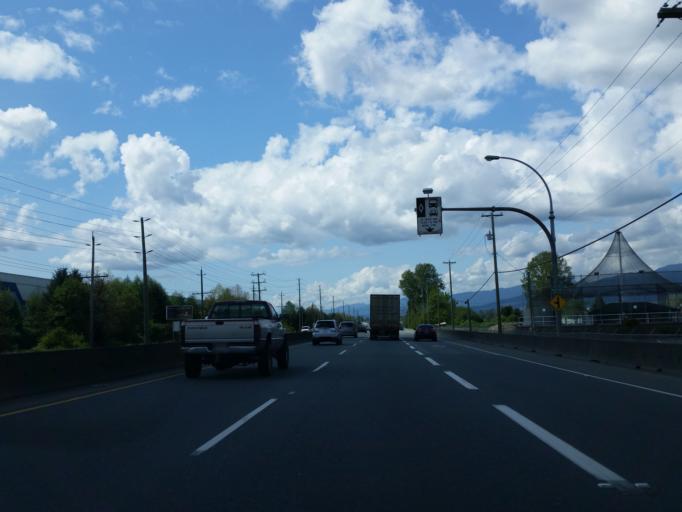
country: CA
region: British Columbia
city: Pitt Meadows
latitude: 49.2331
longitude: -122.6943
